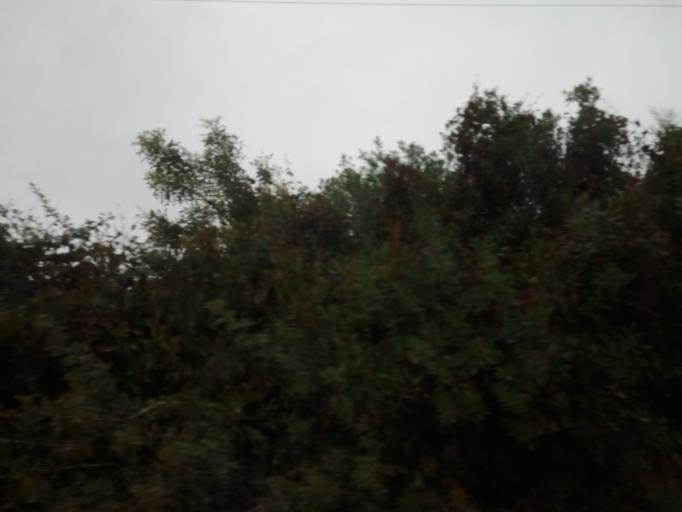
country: DZ
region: Tipaza
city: Tipasa
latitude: 36.5769
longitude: 2.5507
